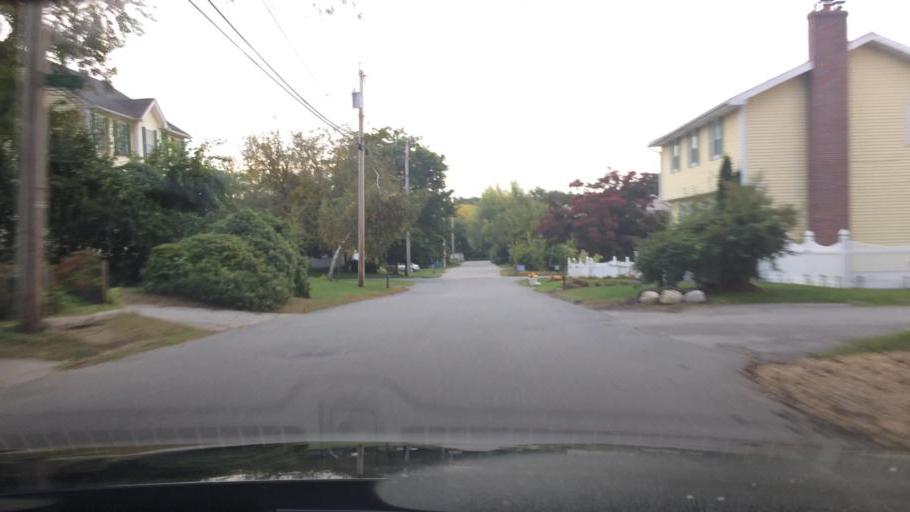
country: US
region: Massachusetts
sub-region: Essex County
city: North Andover
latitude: 42.7338
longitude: -71.1274
